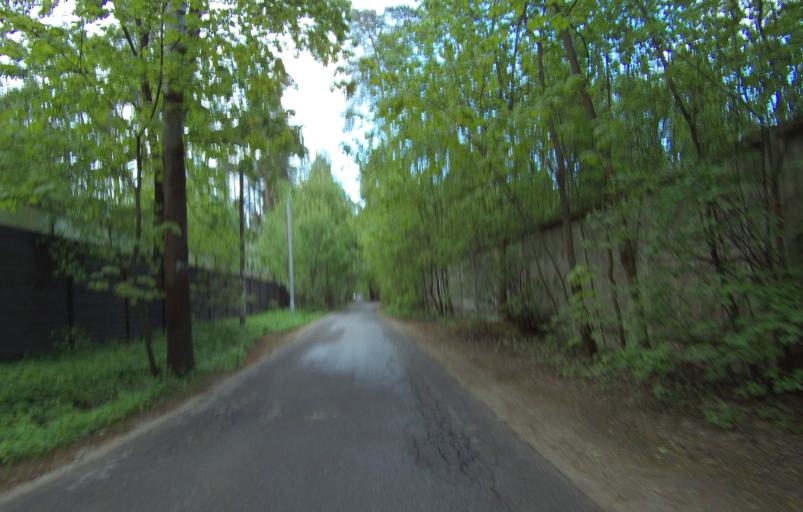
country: RU
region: Moskovskaya
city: Kratovo
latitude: 55.5996
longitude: 38.1684
